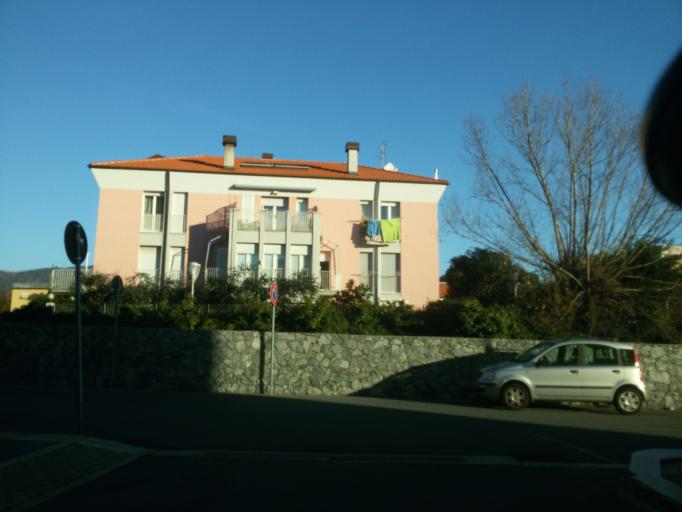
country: IT
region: Liguria
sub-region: Provincia di Savona
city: Valleggia
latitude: 44.2942
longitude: 8.4505
